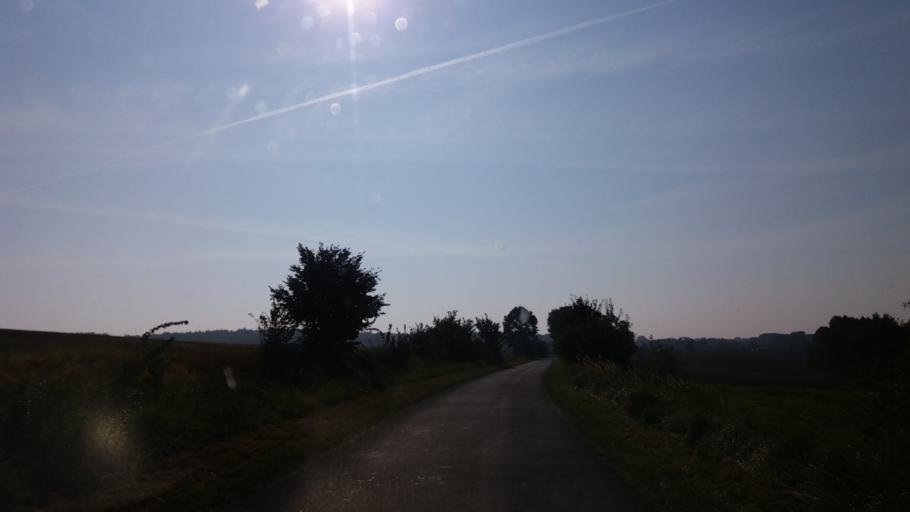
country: PL
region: West Pomeranian Voivodeship
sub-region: Powiat choszczenski
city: Pelczyce
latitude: 53.0045
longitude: 15.3589
